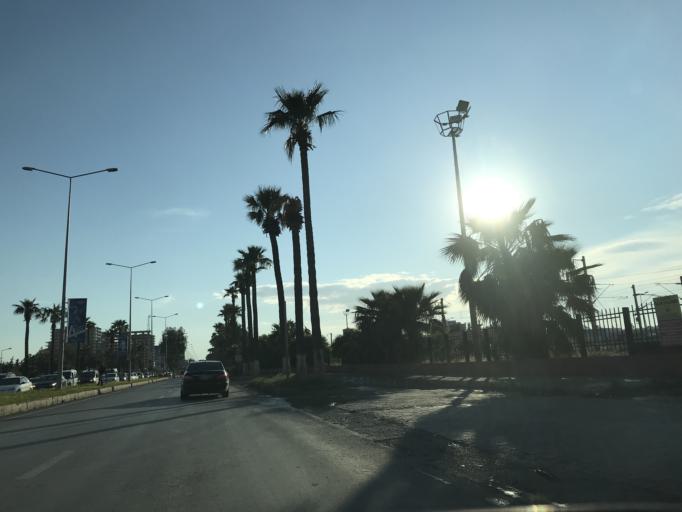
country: TR
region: Hatay
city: Iskenderun
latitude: 36.5894
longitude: 36.1881
